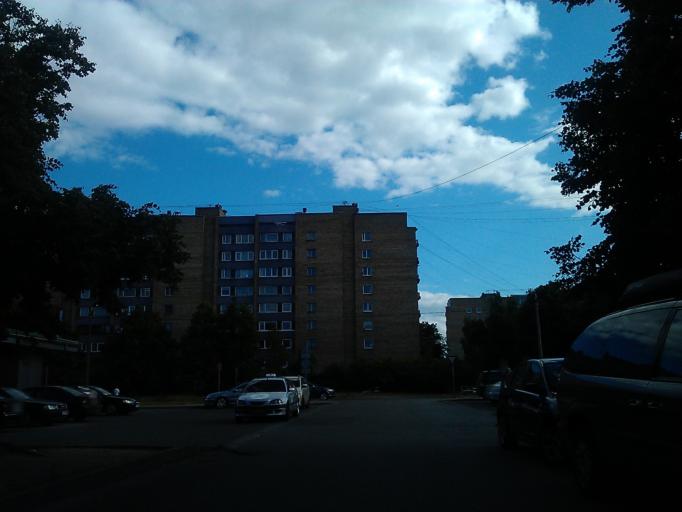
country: LV
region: Riga
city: Jaunciems
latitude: 56.9667
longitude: 24.1816
